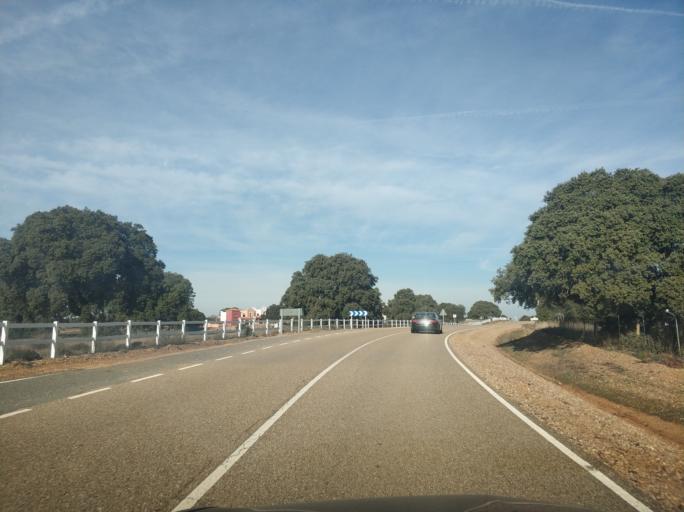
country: ES
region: Castille and Leon
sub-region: Provincia de Salamanca
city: San Pedro del Valle
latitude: 41.0087
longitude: -5.8503
